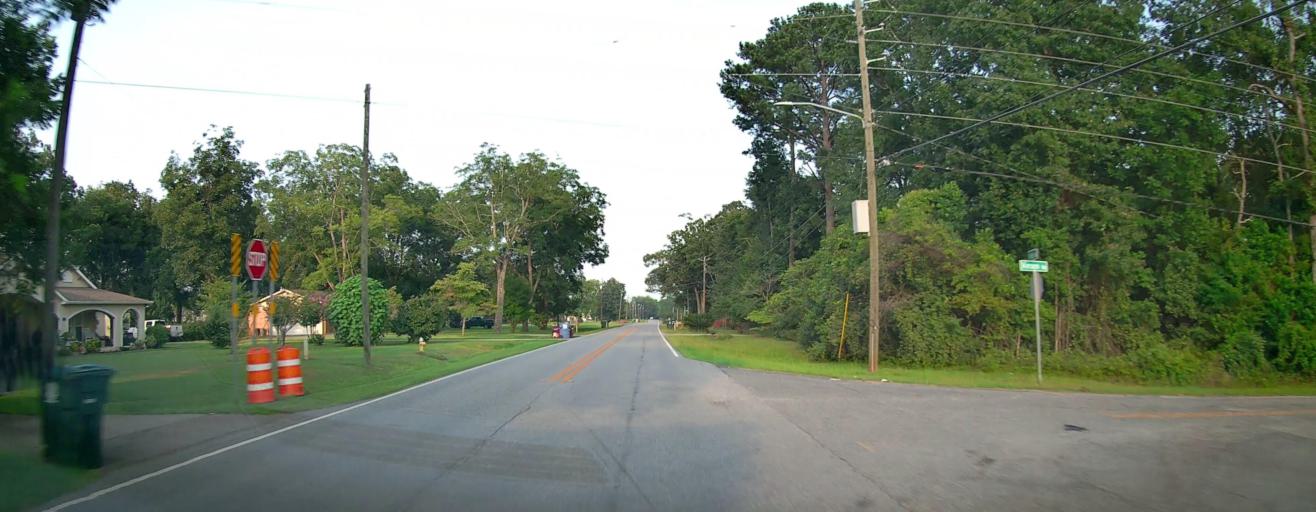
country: US
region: Georgia
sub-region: Houston County
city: Centerville
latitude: 32.7324
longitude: -83.6893
